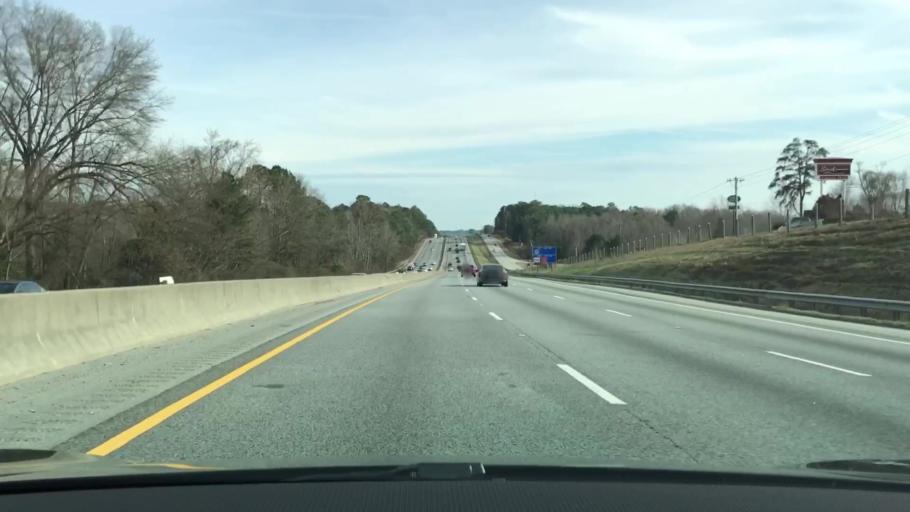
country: US
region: Georgia
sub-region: Newton County
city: Porterdale
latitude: 33.6268
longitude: -83.9428
